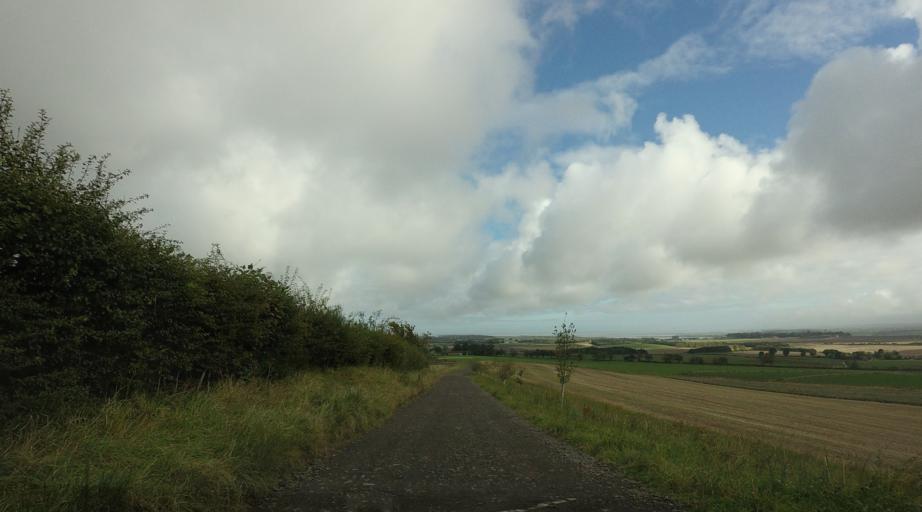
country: GB
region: Scotland
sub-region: Fife
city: Balmullo
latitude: 56.3734
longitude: -2.9435
